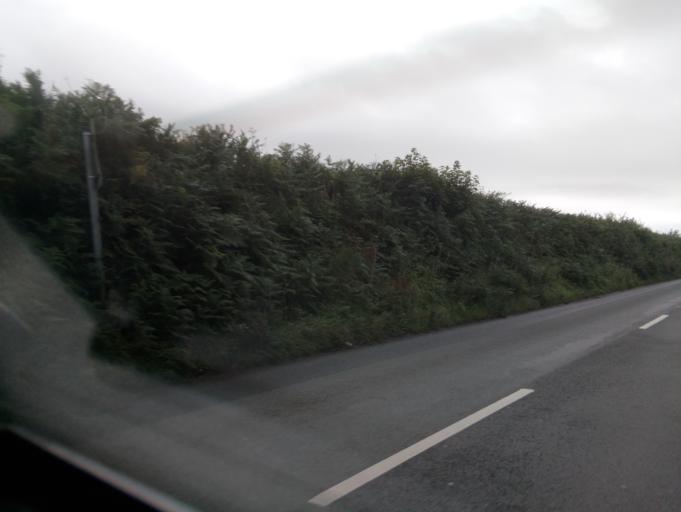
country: GB
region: England
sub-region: Devon
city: Kingsbridge
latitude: 50.2955
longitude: -3.7908
